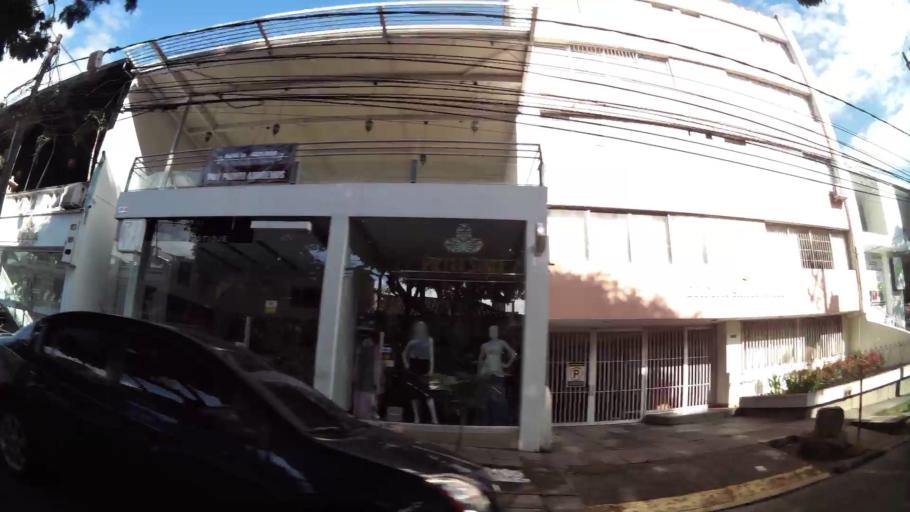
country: CO
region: Valle del Cauca
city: Cali
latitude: 3.4585
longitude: -76.5350
